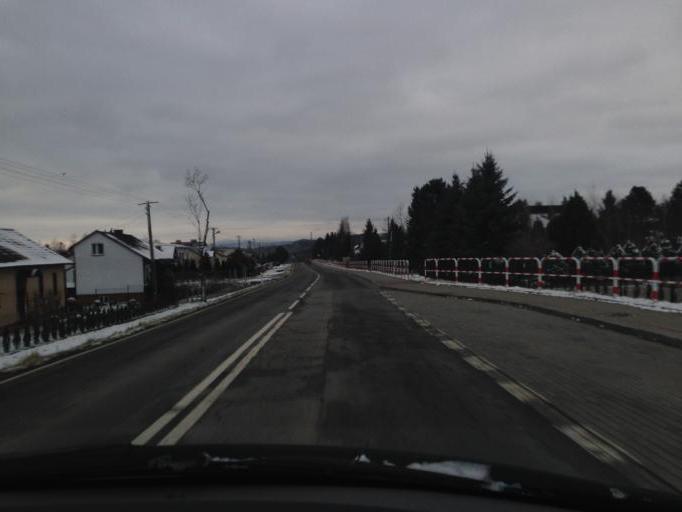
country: PL
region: Lesser Poland Voivodeship
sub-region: Powiat gorlicki
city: Gorlice
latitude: 49.7043
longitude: 21.1379
